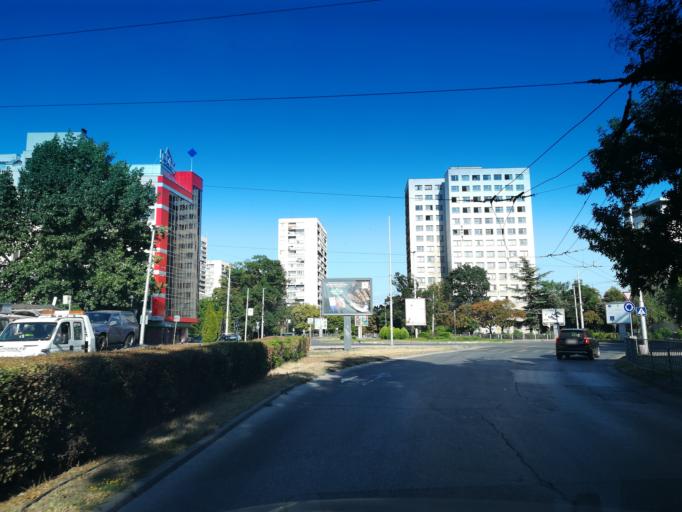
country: BG
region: Plovdiv
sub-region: Obshtina Plovdiv
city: Plovdiv
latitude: 42.1629
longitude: 24.7463
